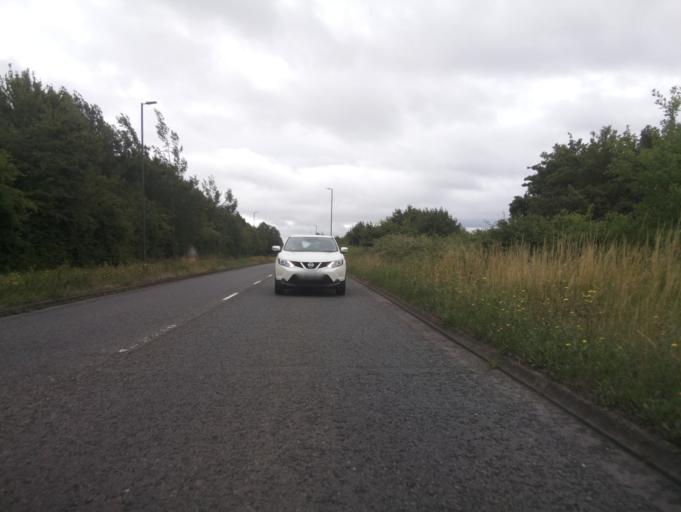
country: GB
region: England
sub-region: Gloucestershire
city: Tewkesbury
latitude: 51.9894
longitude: -2.1465
